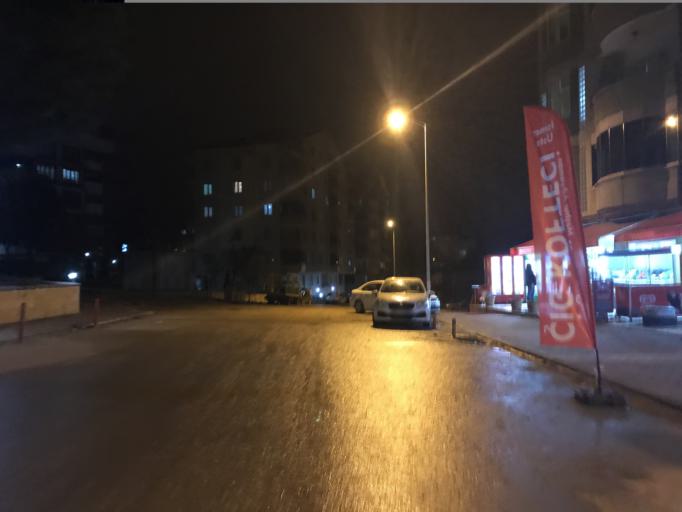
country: TR
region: Karabuk
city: Safranbolu
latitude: 41.2576
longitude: 32.6766
